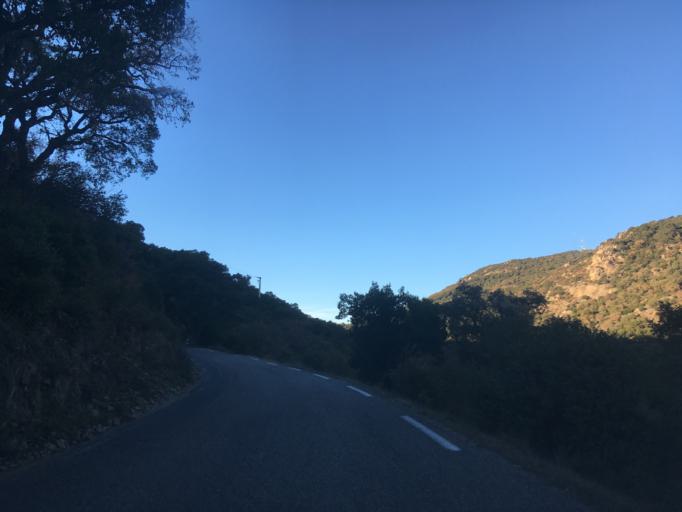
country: FR
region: Provence-Alpes-Cote d'Azur
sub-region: Departement du Var
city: Le Plan-de-la-Tour
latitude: 43.3020
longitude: 6.5564
